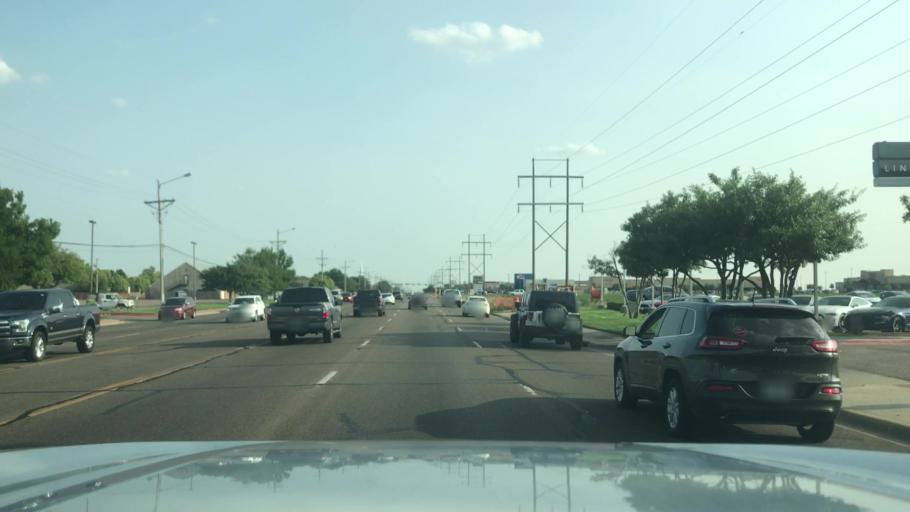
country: US
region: Texas
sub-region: Potter County
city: Amarillo
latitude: 35.1748
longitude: -101.9383
